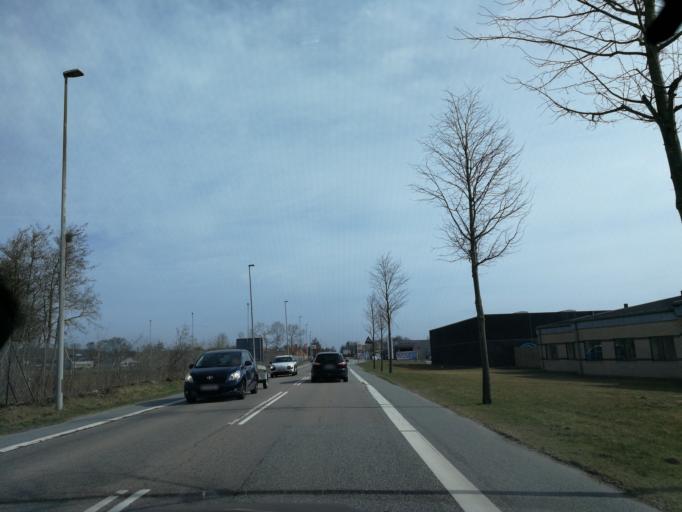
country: DK
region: North Denmark
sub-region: Alborg Kommune
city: Vodskov
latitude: 57.1011
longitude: 10.0197
